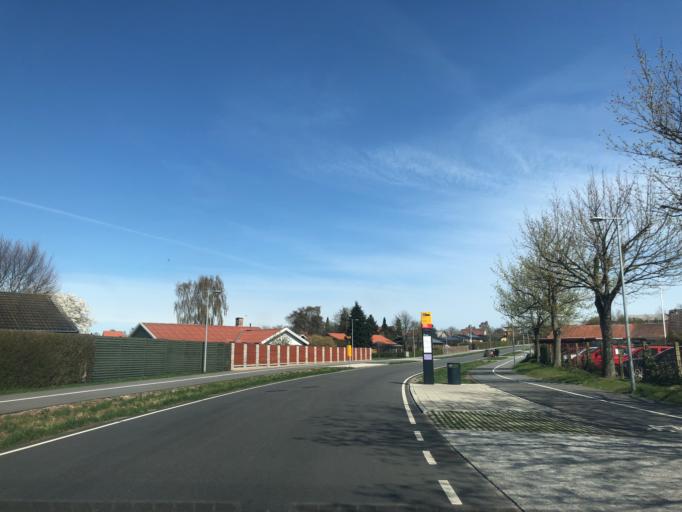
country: DK
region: Zealand
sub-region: Ringsted Kommune
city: Ringsted
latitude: 55.4311
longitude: 11.7838
